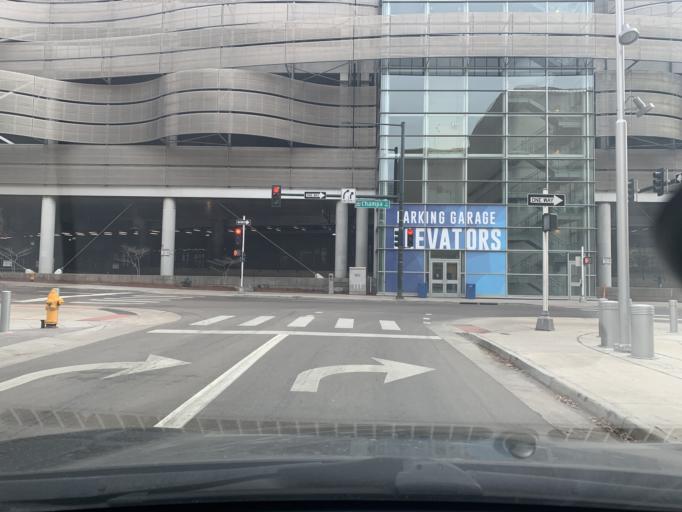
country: US
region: Colorado
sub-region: Denver County
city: Denver
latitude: 39.7439
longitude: -104.9978
